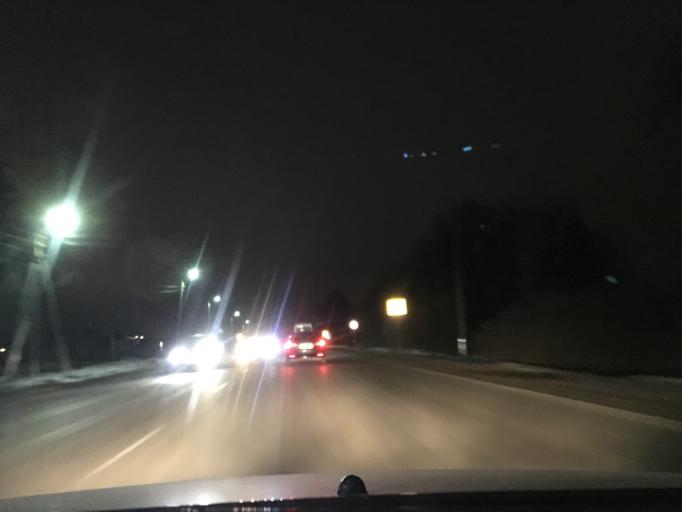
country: RU
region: Tula
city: Kosaya Gora
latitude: 54.1027
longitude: 37.5521
